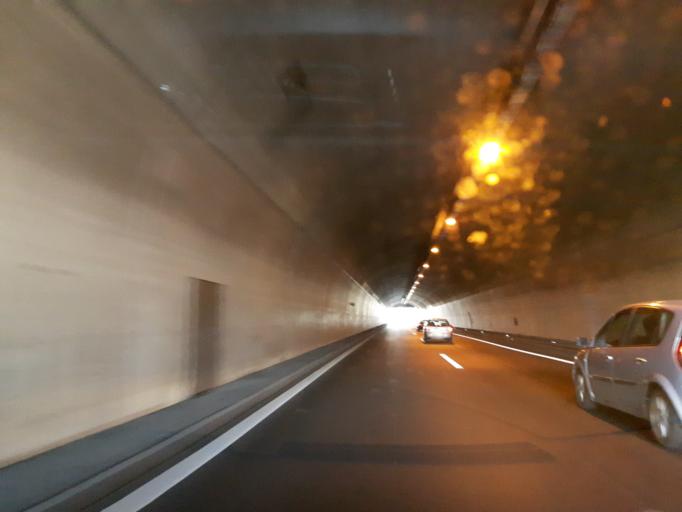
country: CH
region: Lucerne
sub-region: Sursee District
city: Sursee
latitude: 47.1762
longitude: 8.1236
